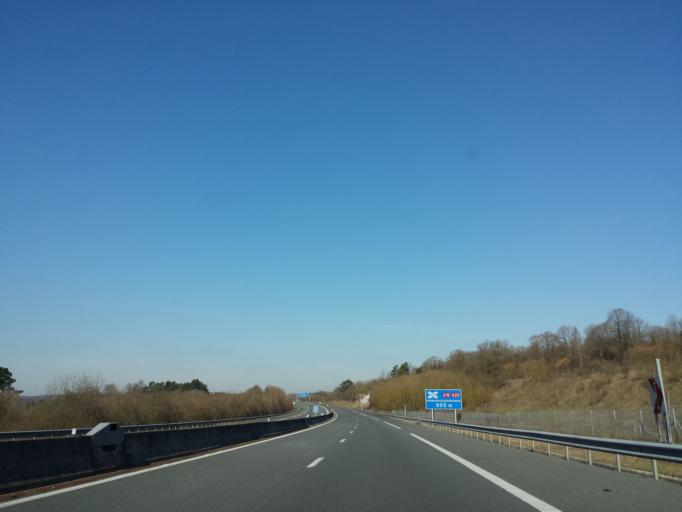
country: FR
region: Picardie
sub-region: Departement de la Somme
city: Saleux
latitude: 49.8389
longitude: 2.2516
